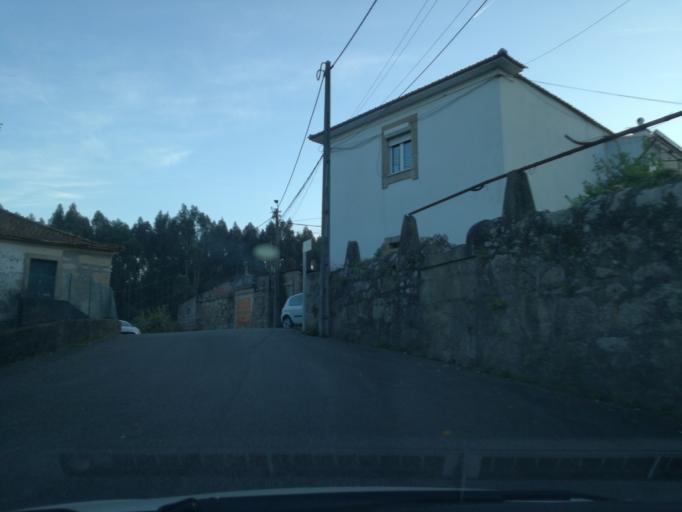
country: PT
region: Porto
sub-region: Maia
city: Anta
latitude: 41.2723
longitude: -8.6213
